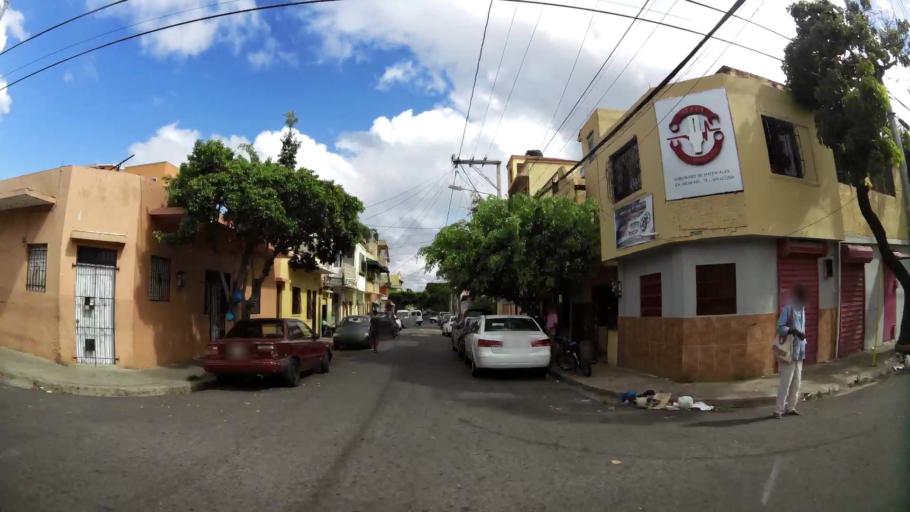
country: DO
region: Nacional
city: San Carlos
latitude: 18.4824
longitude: -69.9014
